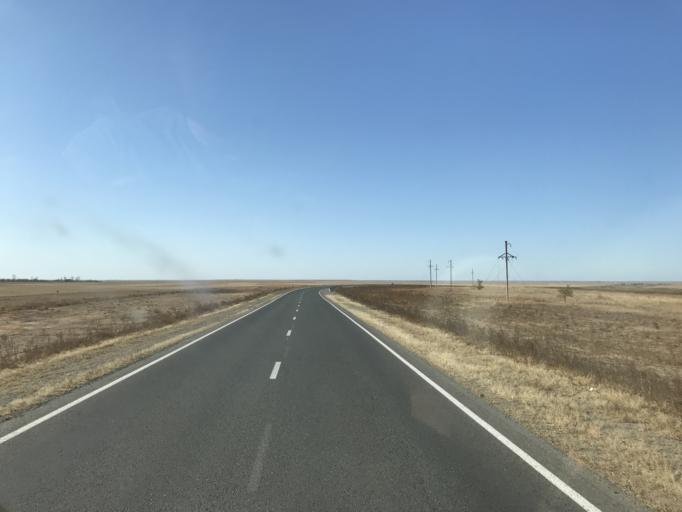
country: KZ
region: Pavlodar
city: Kurchatov
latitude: 50.9618
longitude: 79.3312
